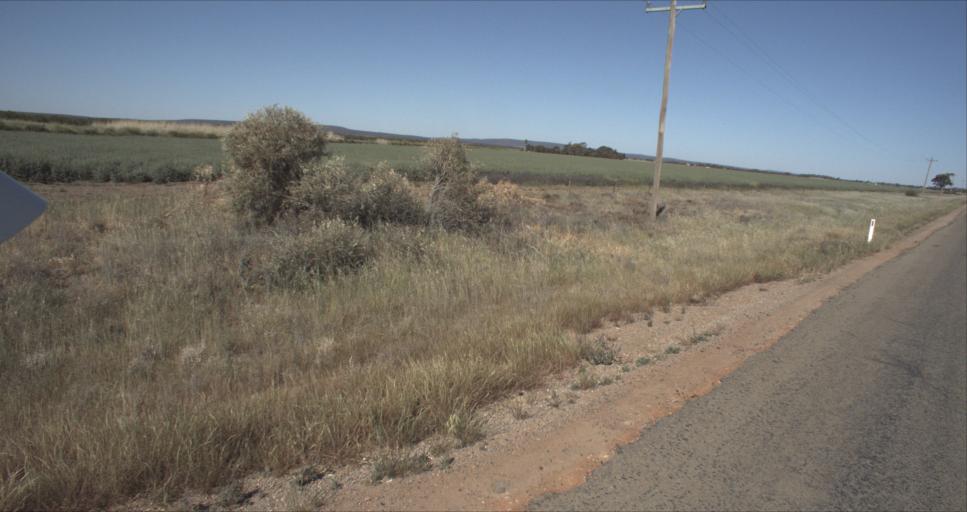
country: AU
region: New South Wales
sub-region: Leeton
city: Leeton
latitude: -34.4806
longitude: 146.3708
